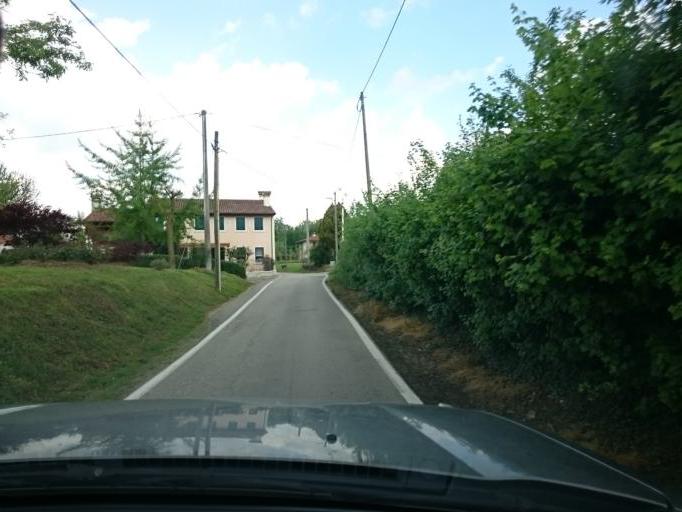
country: IT
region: Veneto
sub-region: Provincia di Vicenza
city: Villaggio Montegrappa
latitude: 45.5233
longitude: 11.5823
